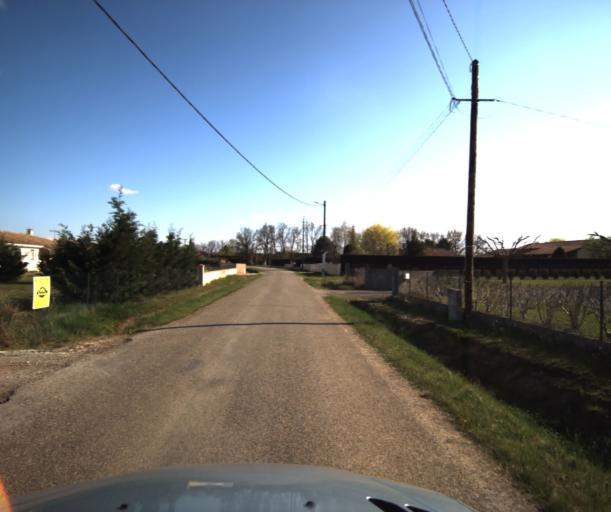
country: FR
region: Midi-Pyrenees
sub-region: Departement du Tarn-et-Garonne
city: Campsas
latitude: 43.9359
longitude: 1.3057
